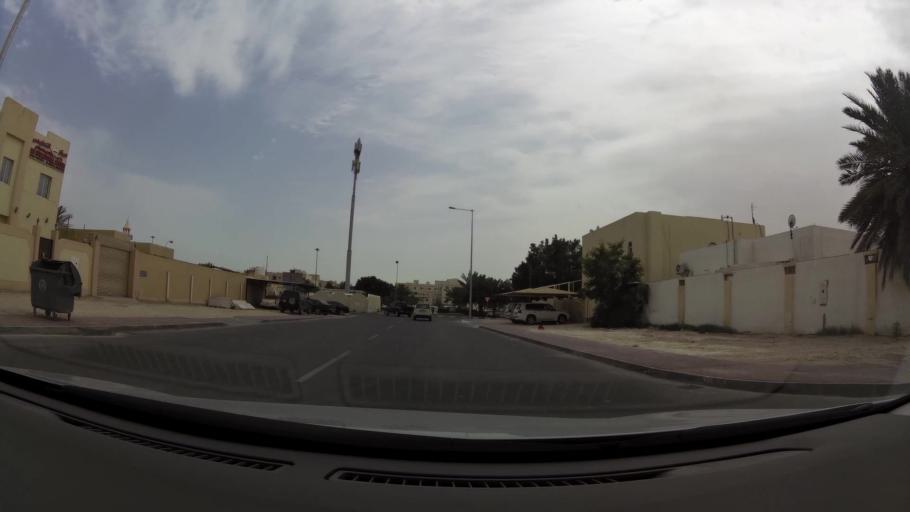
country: QA
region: Baladiyat ar Rayyan
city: Ar Rayyan
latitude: 25.3223
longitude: 51.4708
